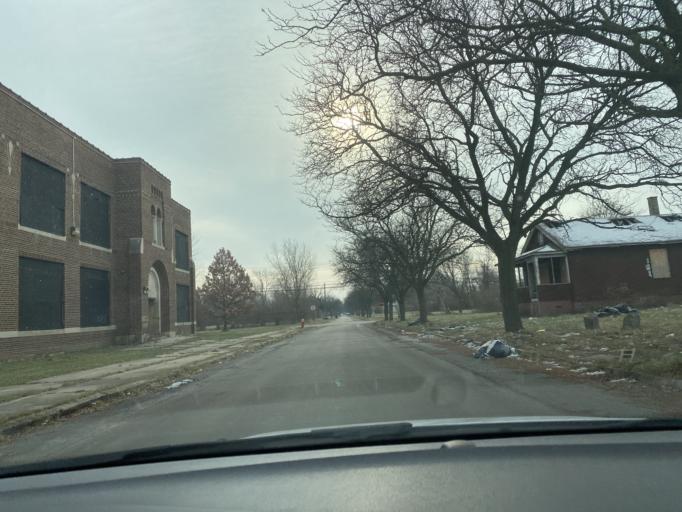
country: US
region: Michigan
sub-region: Wayne County
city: Highland Park
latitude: 42.3739
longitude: -83.1329
